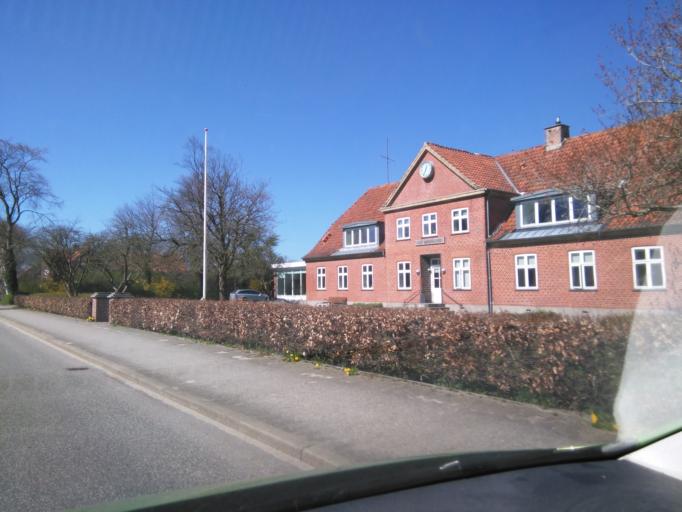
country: DK
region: South Denmark
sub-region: Varde Kommune
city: Oksbol
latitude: 55.6236
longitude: 8.3698
